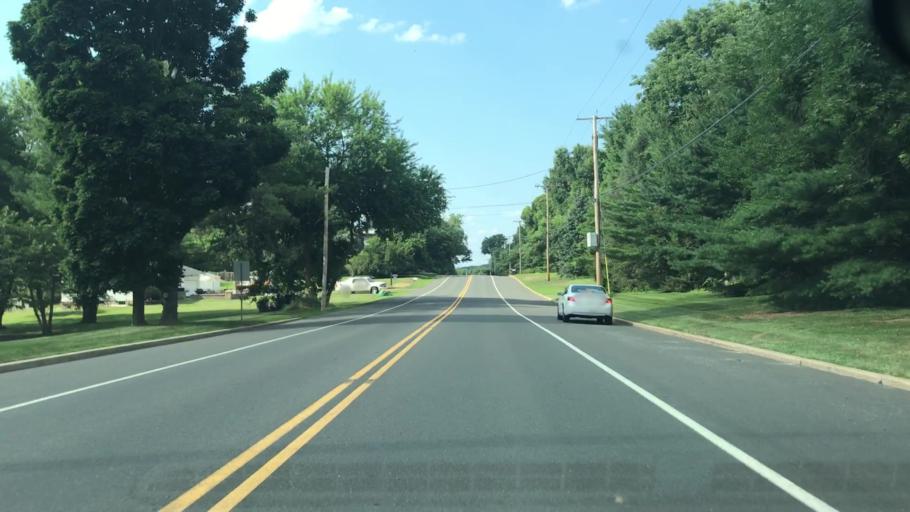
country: US
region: New Jersey
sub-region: Hunterdon County
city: Flemington
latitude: 40.5069
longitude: -74.8081
